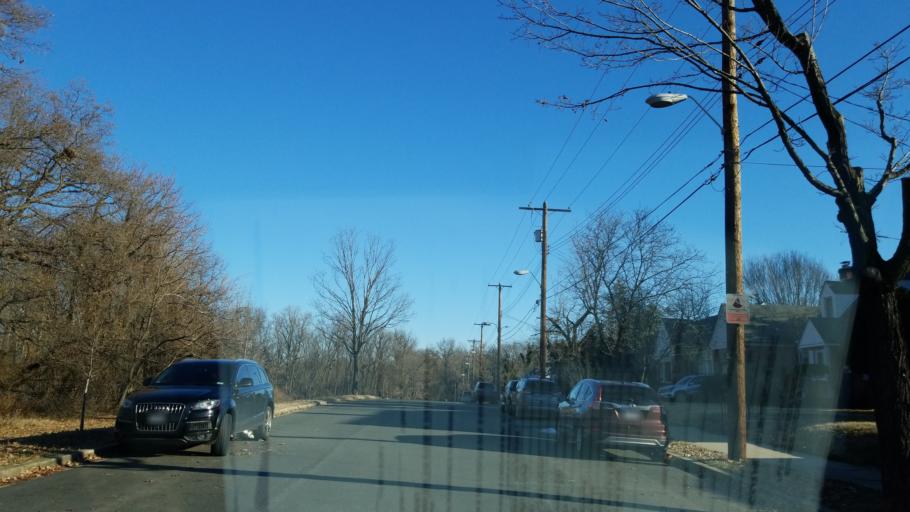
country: US
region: Maryland
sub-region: Prince George's County
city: Glassmanor
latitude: 38.8331
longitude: -77.0112
